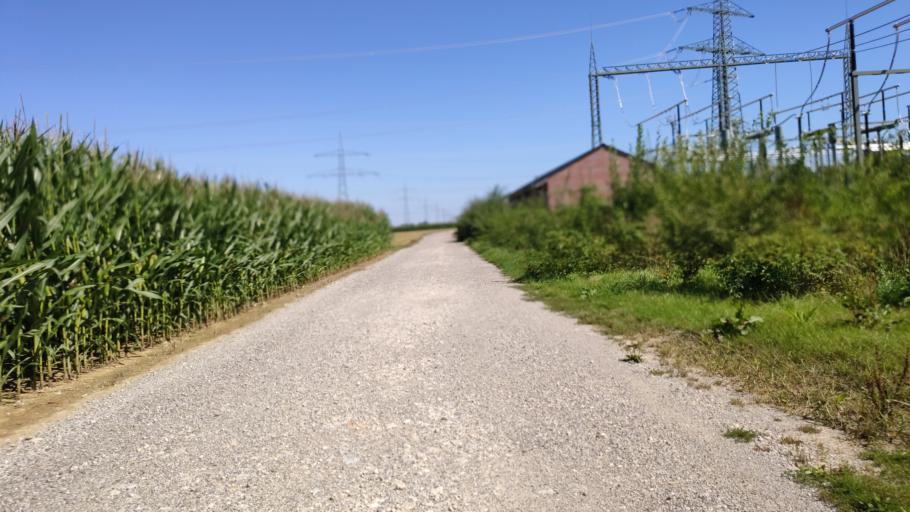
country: DE
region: Bavaria
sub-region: Swabia
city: Oberottmarshausen
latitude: 48.2373
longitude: 10.8374
